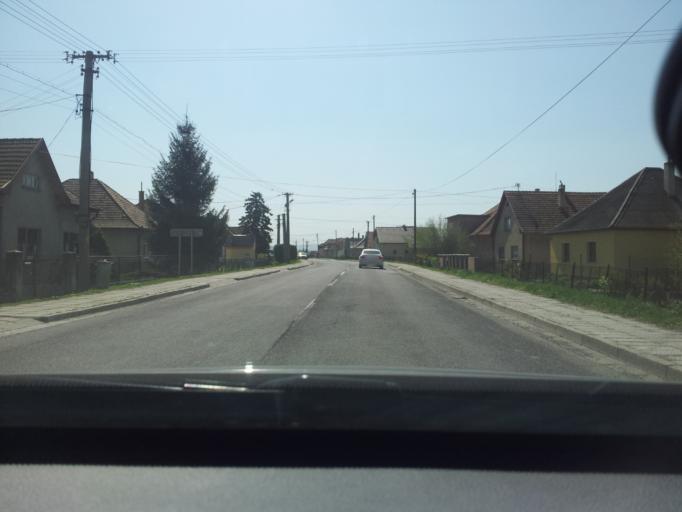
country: SK
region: Nitriansky
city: Banovce nad Bebravou
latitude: 48.6654
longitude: 18.2613
